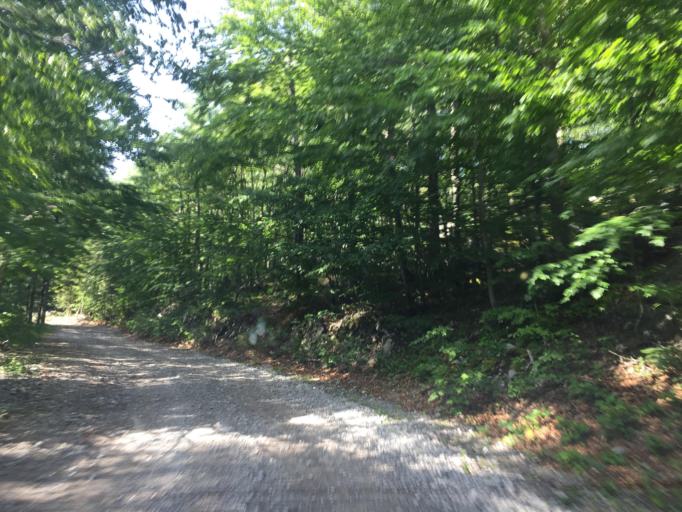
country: HR
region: Primorsko-Goranska
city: Podhum
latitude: 45.4558
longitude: 14.5431
